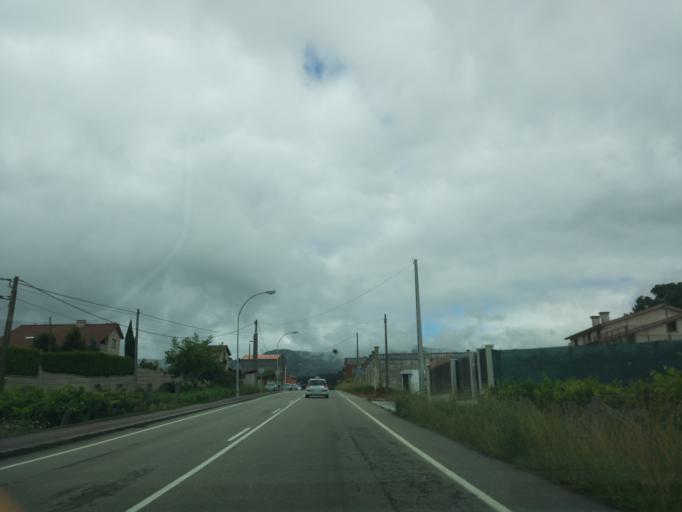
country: ES
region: Galicia
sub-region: Provincia da Coruna
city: Boiro
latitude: 42.6446
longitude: -8.8720
